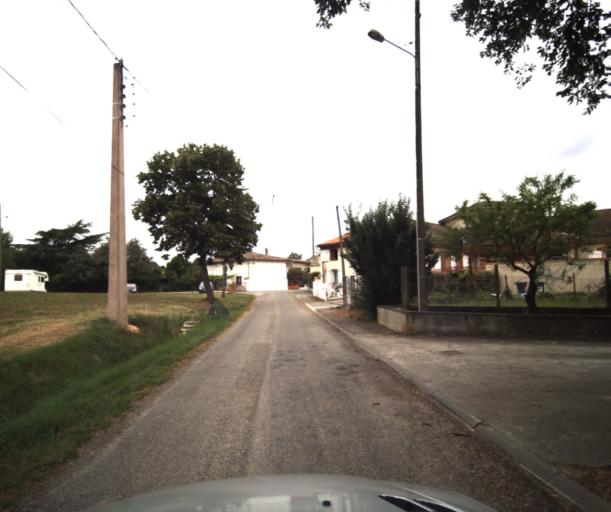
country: FR
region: Midi-Pyrenees
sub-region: Departement de la Haute-Garonne
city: Pinsaguel
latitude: 43.5071
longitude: 1.3855
